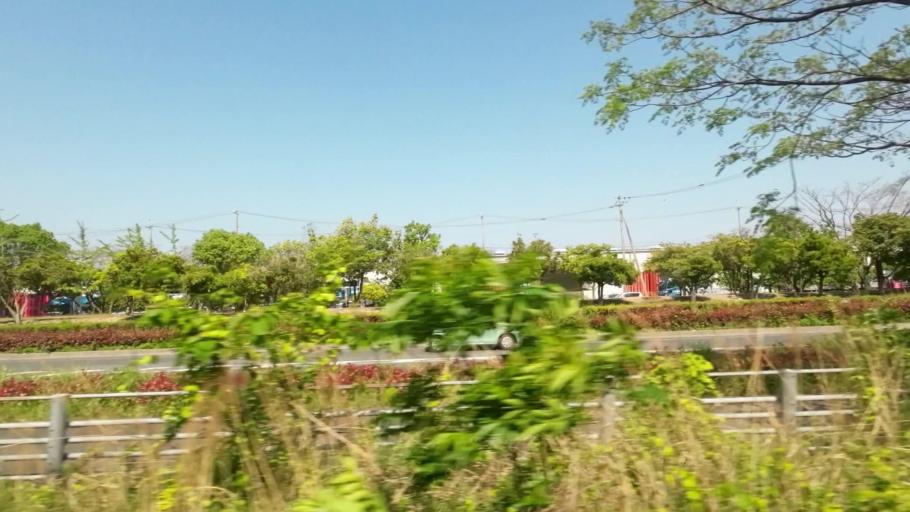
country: JP
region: Ehime
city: Kawanoecho
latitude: 34.0280
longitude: 133.5829
